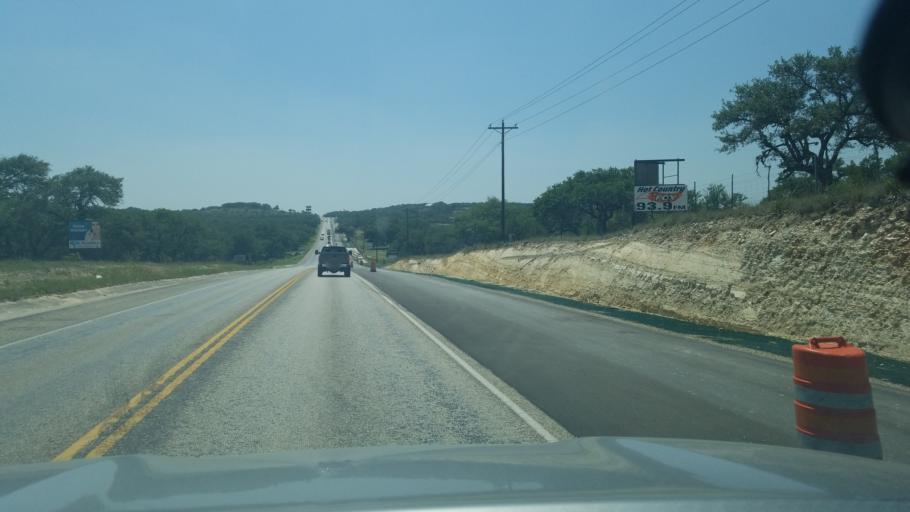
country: US
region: Texas
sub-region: Bexar County
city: Fair Oaks Ranch
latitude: 29.8190
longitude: -98.5925
